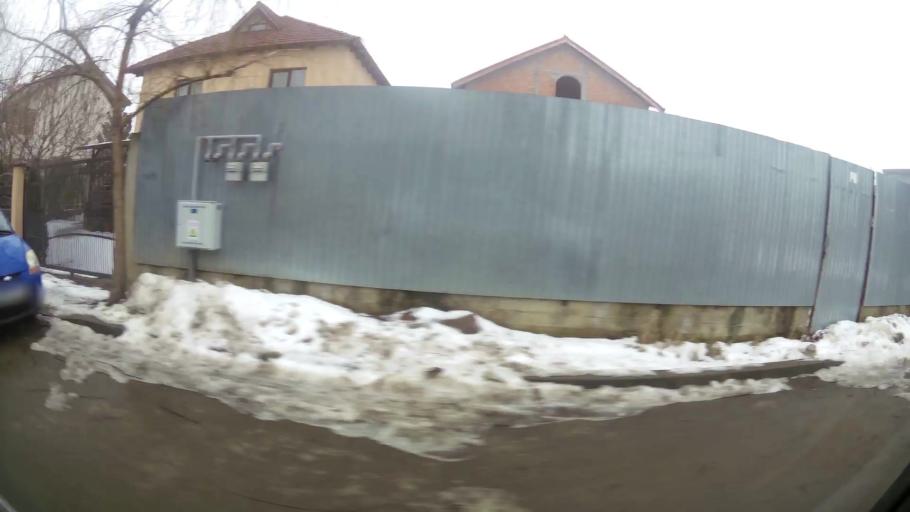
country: RO
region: Ilfov
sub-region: Comuna Chiajna
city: Chiajna
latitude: 44.4543
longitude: 25.9796
